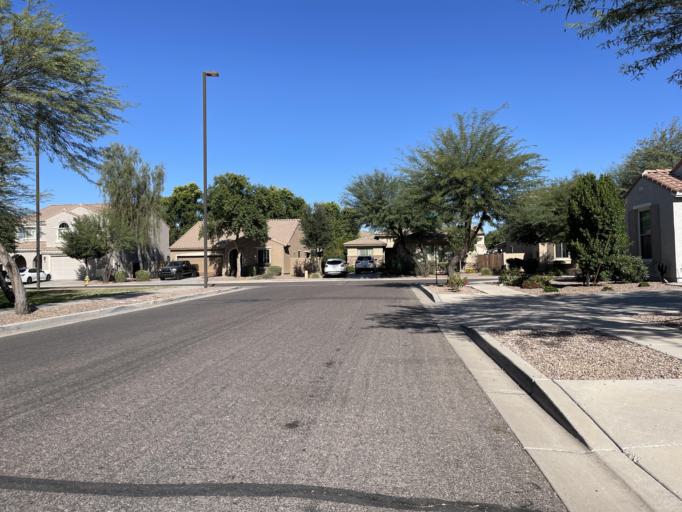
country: US
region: Arizona
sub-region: Maricopa County
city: Queen Creek
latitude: 33.2822
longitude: -111.6930
